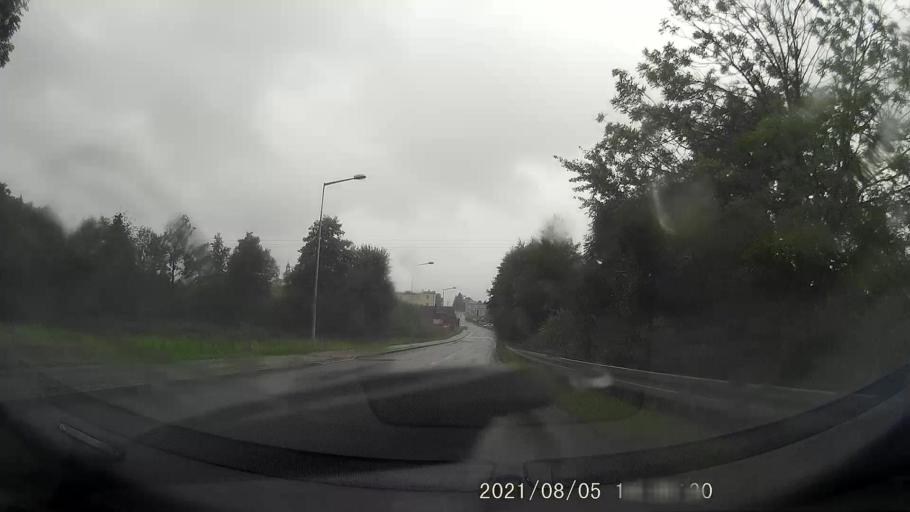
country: PL
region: Opole Voivodeship
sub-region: Powiat nyski
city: Lambinowice
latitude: 50.4672
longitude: 17.5041
